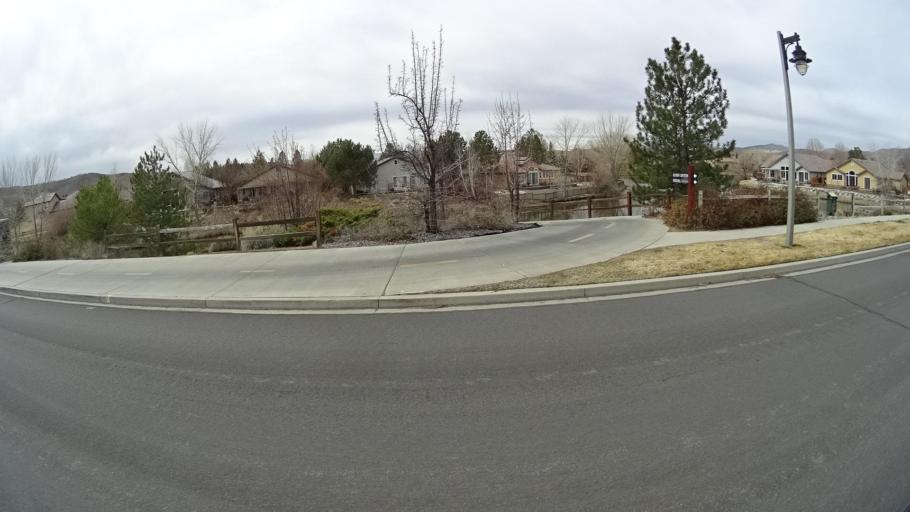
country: US
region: Nevada
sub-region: Washoe County
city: Spanish Springs
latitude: 39.6123
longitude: -119.6900
